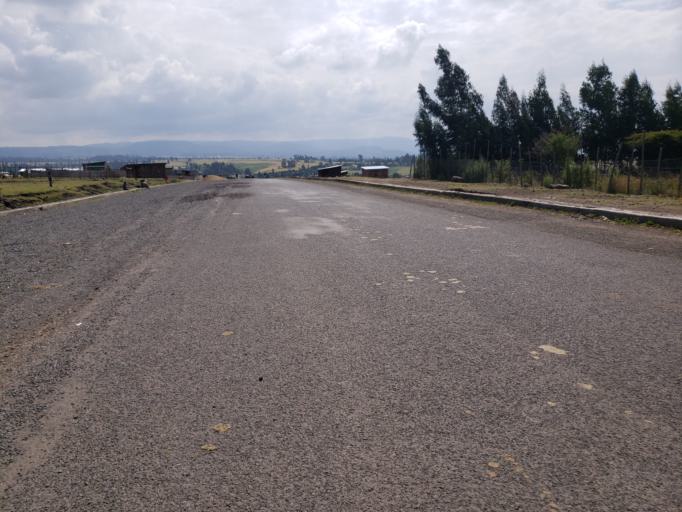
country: ET
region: Oromiya
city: Dodola
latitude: 6.9963
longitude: 39.3907
